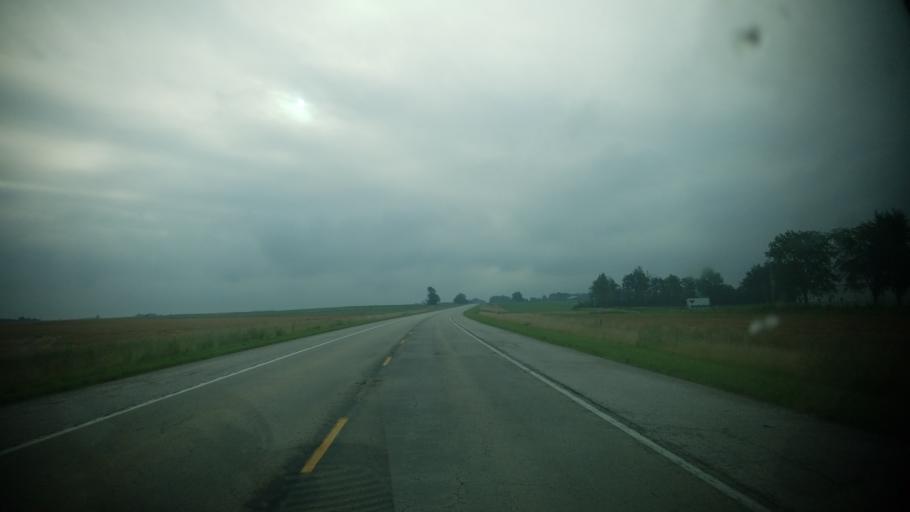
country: US
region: Illinois
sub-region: Clay County
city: Flora
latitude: 38.6769
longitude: -88.4187
